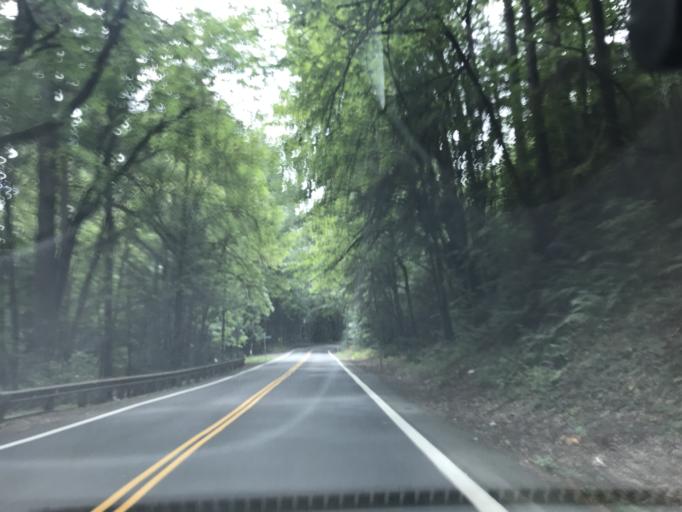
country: US
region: Washington
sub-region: King County
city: Black Diamond
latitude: 47.2849
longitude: -122.0345
